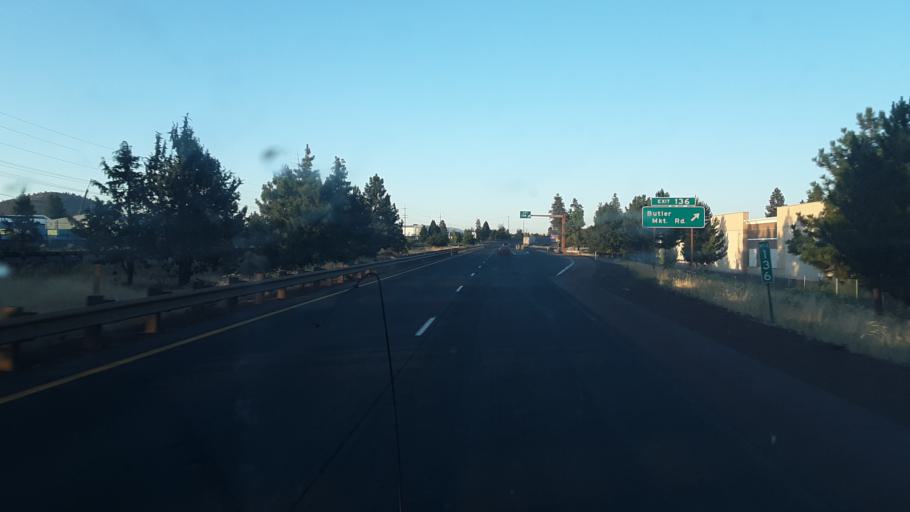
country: US
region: Oregon
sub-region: Deschutes County
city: Bend
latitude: 44.0833
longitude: -121.3013
